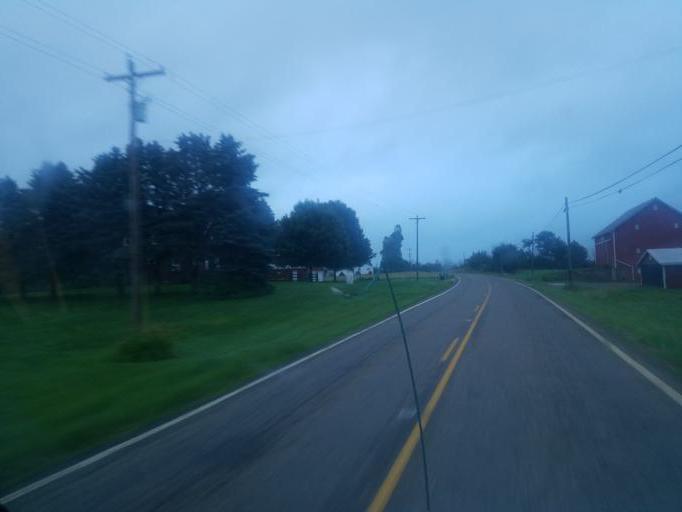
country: US
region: Ohio
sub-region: Columbiana County
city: Salineville
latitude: 40.6172
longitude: -80.9356
